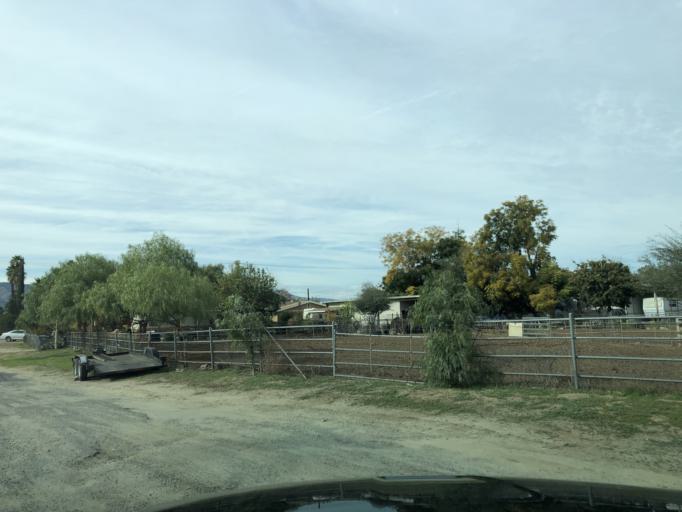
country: US
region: California
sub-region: Riverside County
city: Wildomar
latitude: 33.6210
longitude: -117.2743
